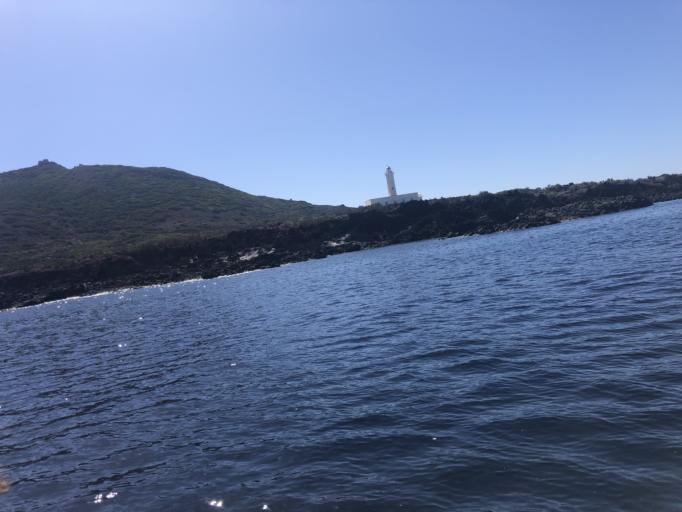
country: IT
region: Sicily
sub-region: Agrigento
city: Lampedusa
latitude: 35.8720
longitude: 12.8814
